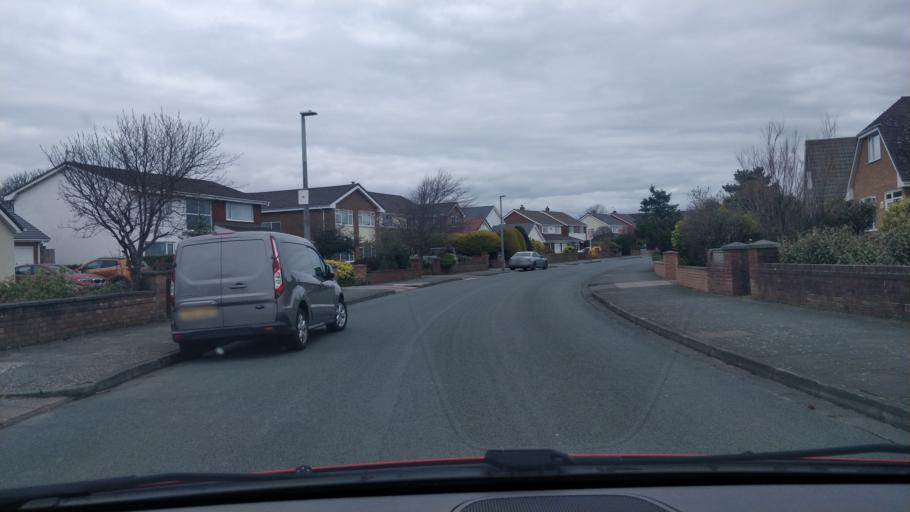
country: GB
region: England
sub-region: Sefton
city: Formby
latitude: 53.6069
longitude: -3.0512
